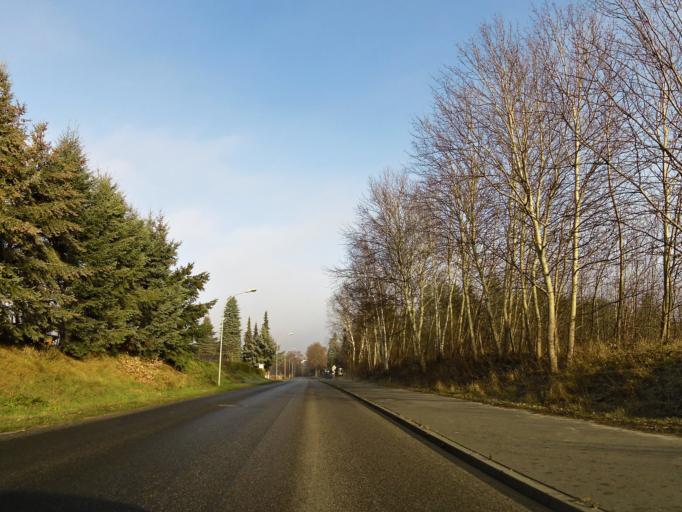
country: DE
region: Brandenburg
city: Werder
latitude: 52.3522
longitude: 12.9059
